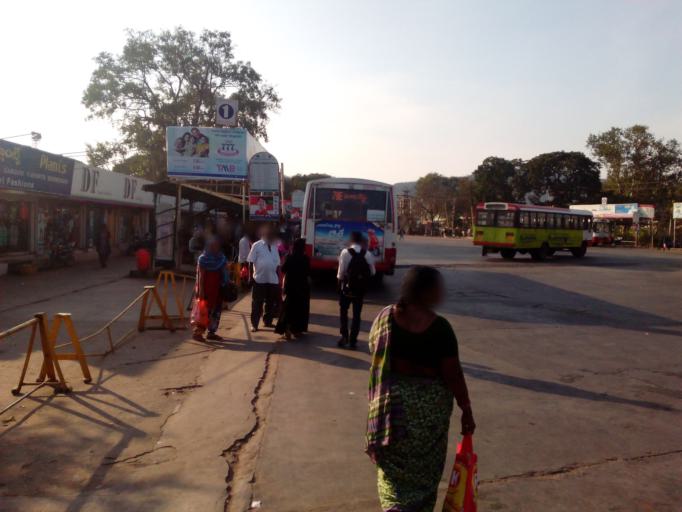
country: IN
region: Andhra Pradesh
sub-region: Krishna
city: Vijayawada
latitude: 16.5096
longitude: 80.6165
